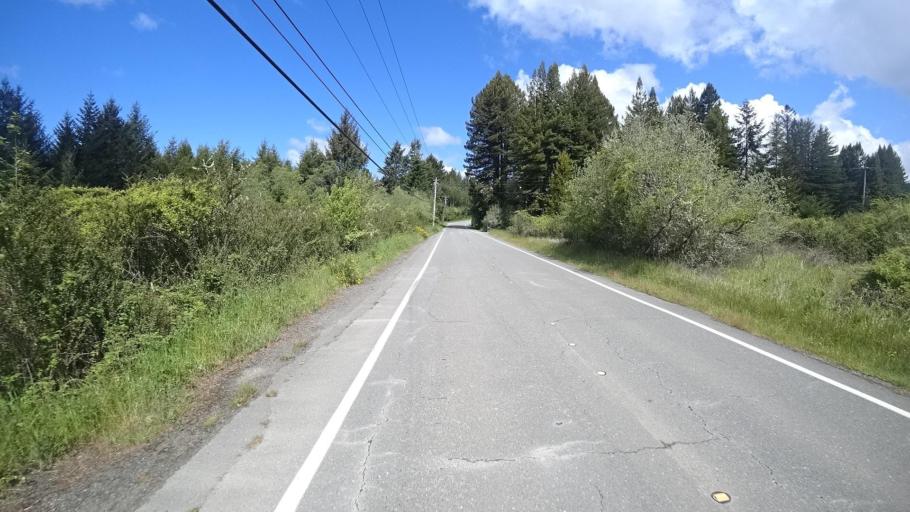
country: US
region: California
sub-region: Humboldt County
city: McKinleyville
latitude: 40.9478
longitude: -124.0308
